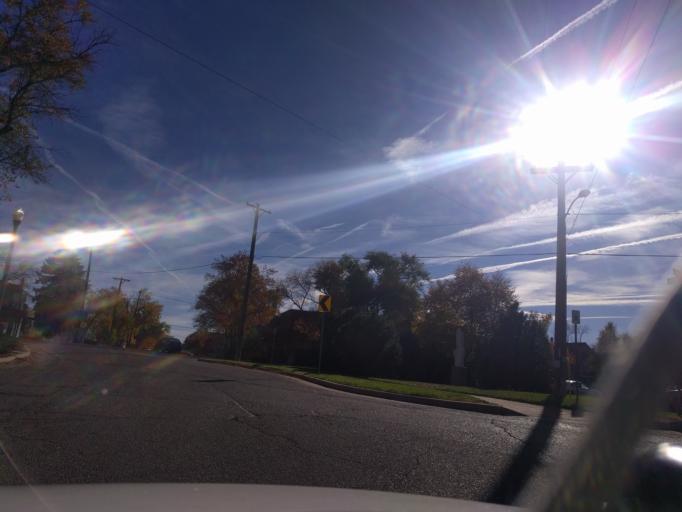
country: US
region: Colorado
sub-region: El Paso County
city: Colorado Springs
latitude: 38.8438
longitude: -104.8255
